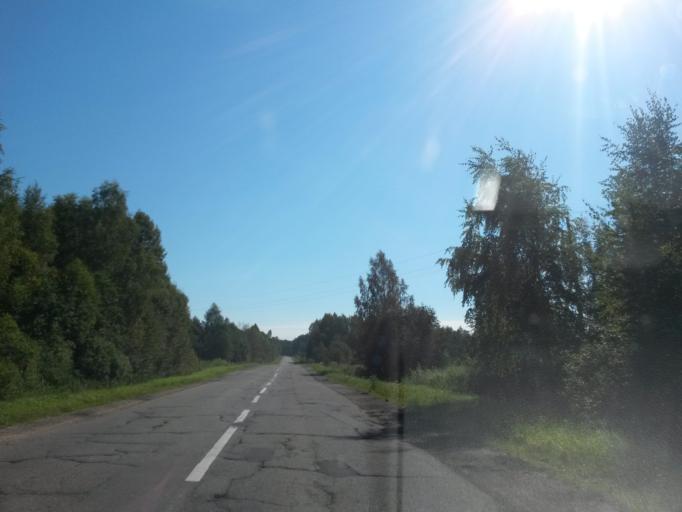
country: RU
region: Jaroslavl
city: Gavrilov-Yam
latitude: 57.3024
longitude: 40.0295
